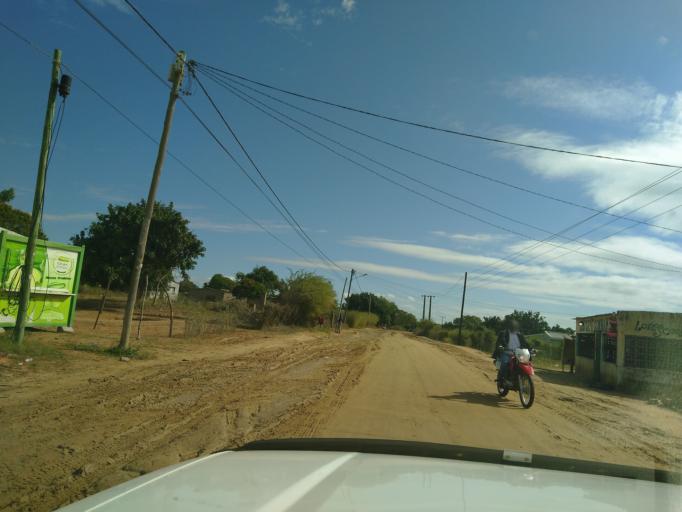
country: MZ
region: Maputo City
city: Maputo
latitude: -26.0031
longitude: 32.5450
